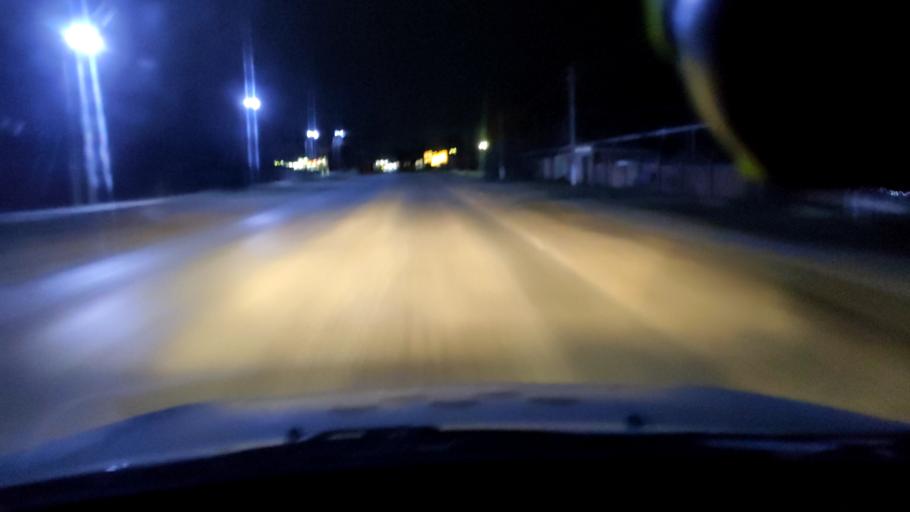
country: RU
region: Samara
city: Podstepki
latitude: 53.6024
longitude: 49.0415
